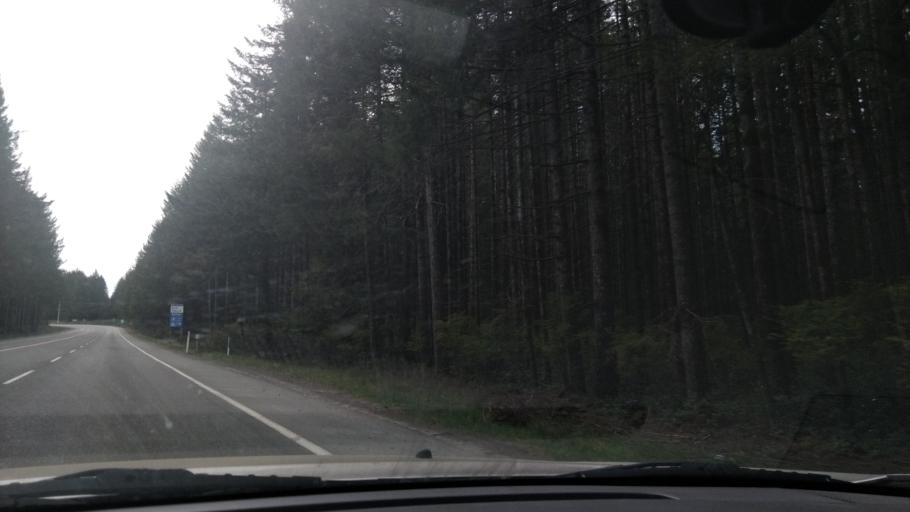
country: CA
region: British Columbia
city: Campbell River
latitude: 50.0362
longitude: -125.3237
